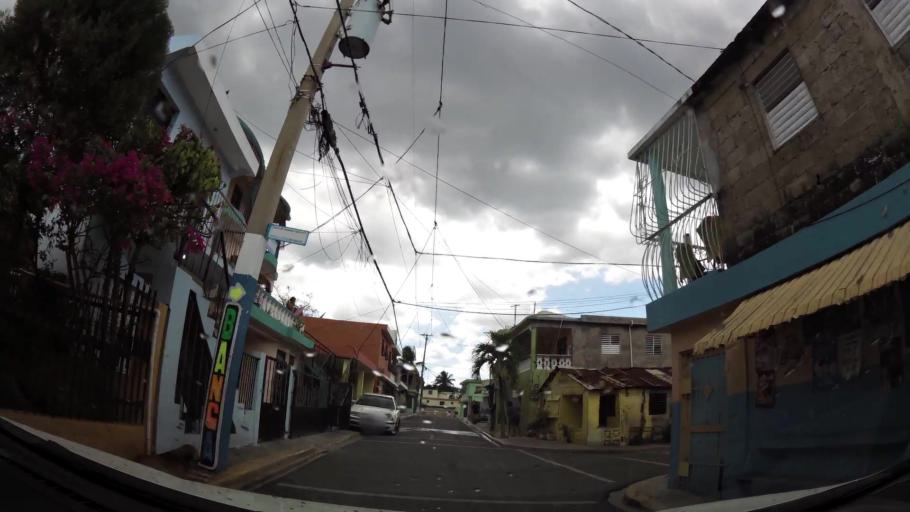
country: DO
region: San Cristobal
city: San Cristobal
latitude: 18.4216
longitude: -70.0922
